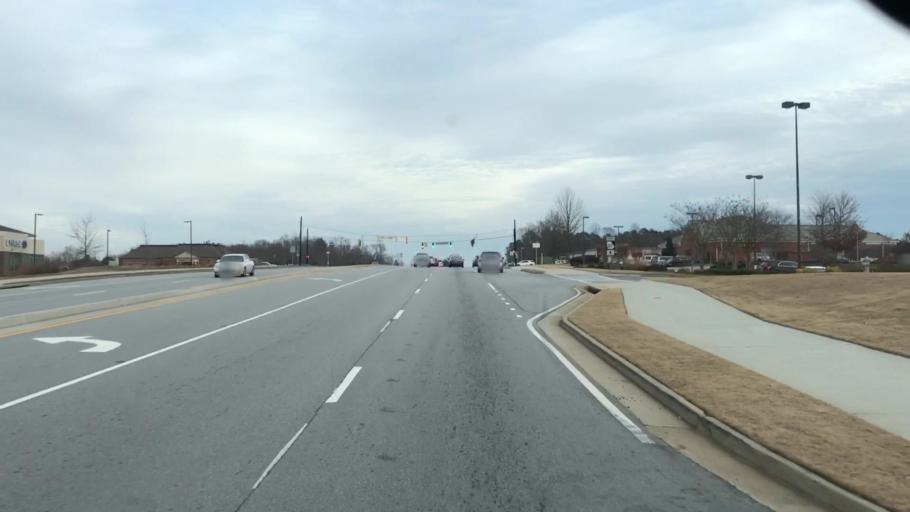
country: US
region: Georgia
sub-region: Hall County
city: Flowery Branch
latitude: 34.1092
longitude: -83.8763
